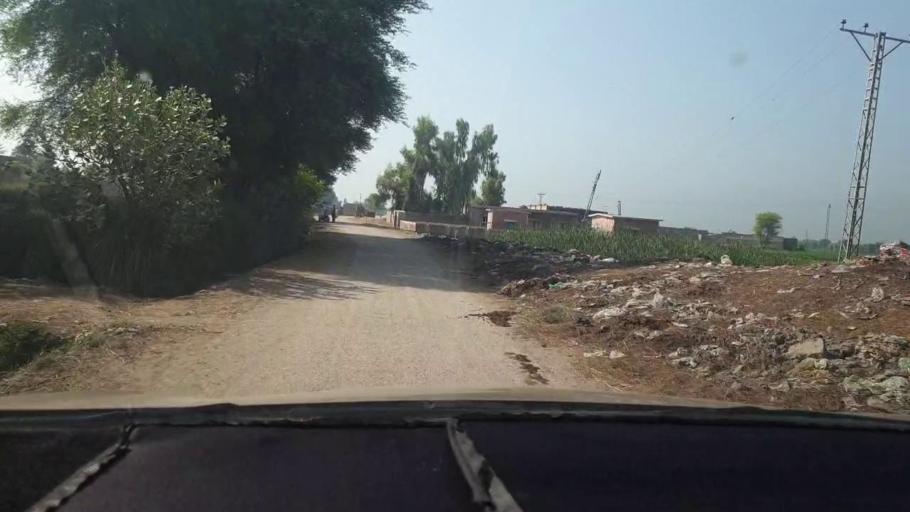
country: PK
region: Sindh
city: Kambar
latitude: 27.6037
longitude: 68.0929
